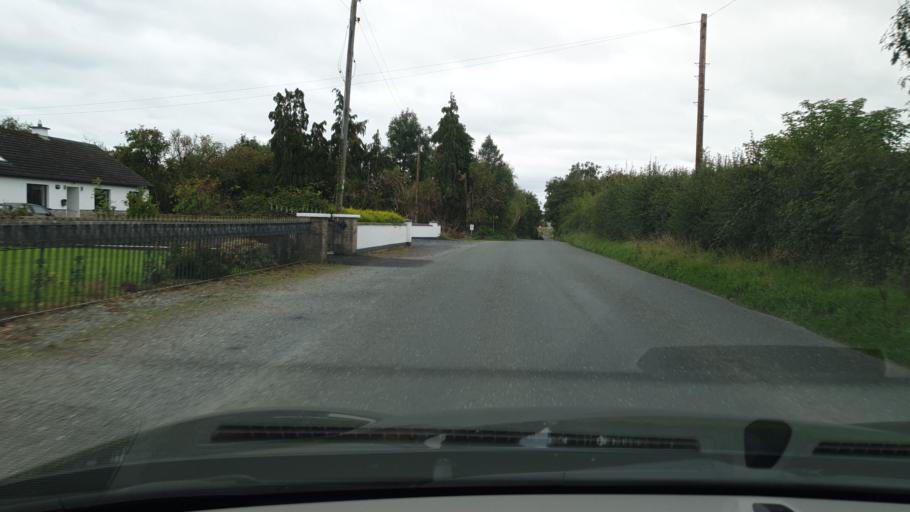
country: IE
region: Leinster
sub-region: Kildare
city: Kilcock
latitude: 53.4029
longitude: -6.6579
